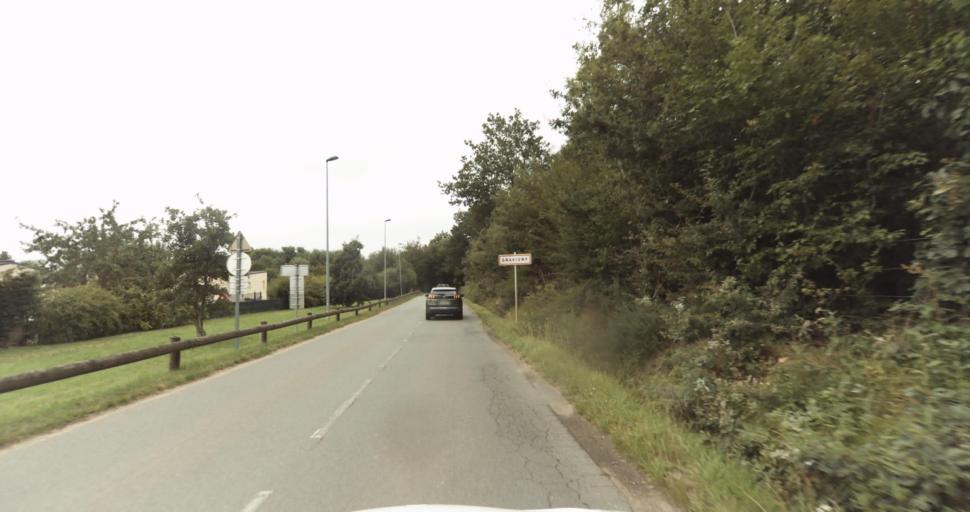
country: FR
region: Haute-Normandie
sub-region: Departement de l'Eure
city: Gravigny
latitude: 49.0363
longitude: 1.1741
